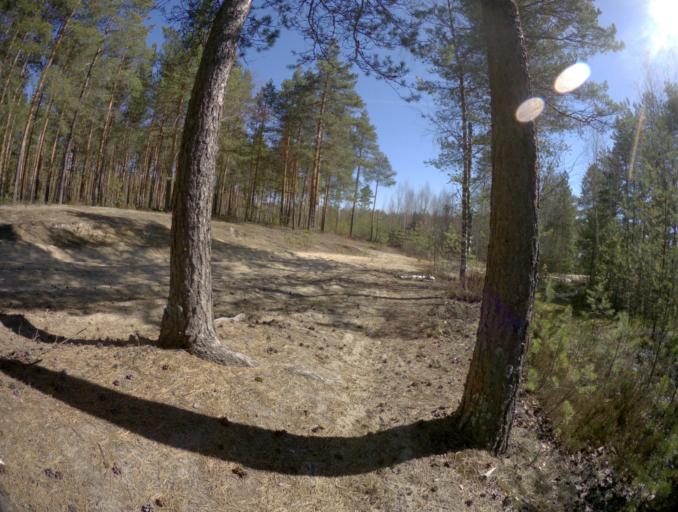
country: RU
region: Vladimir
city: Ivanishchi
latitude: 55.8058
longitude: 40.4210
